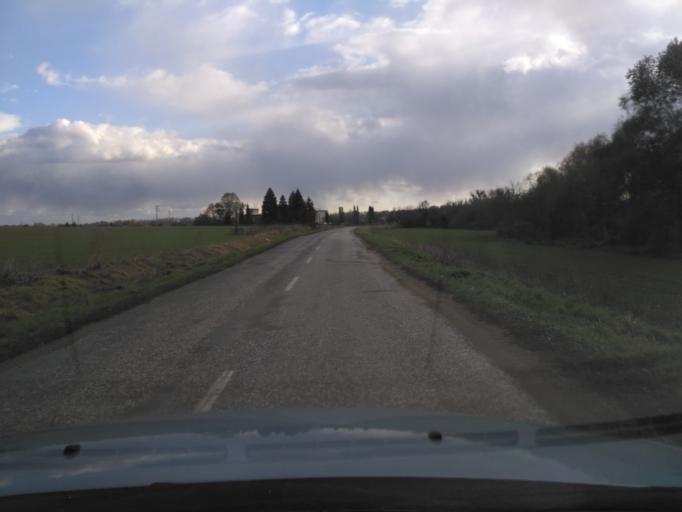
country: HU
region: Borsod-Abauj-Zemplen
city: Satoraljaujhely
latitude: 48.4014
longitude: 21.7093
